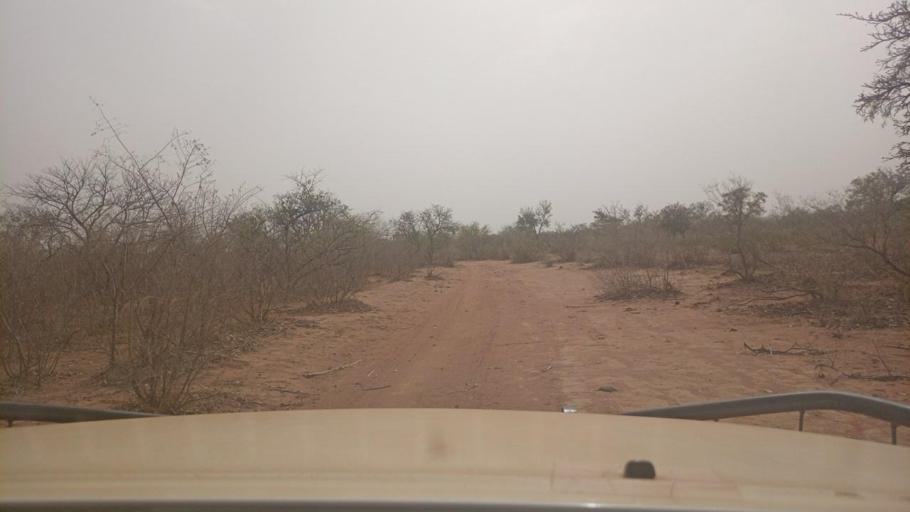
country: BF
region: Boucle du Mouhoun
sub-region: Province des Banwa
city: Salanso
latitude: 12.1607
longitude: -4.2424
